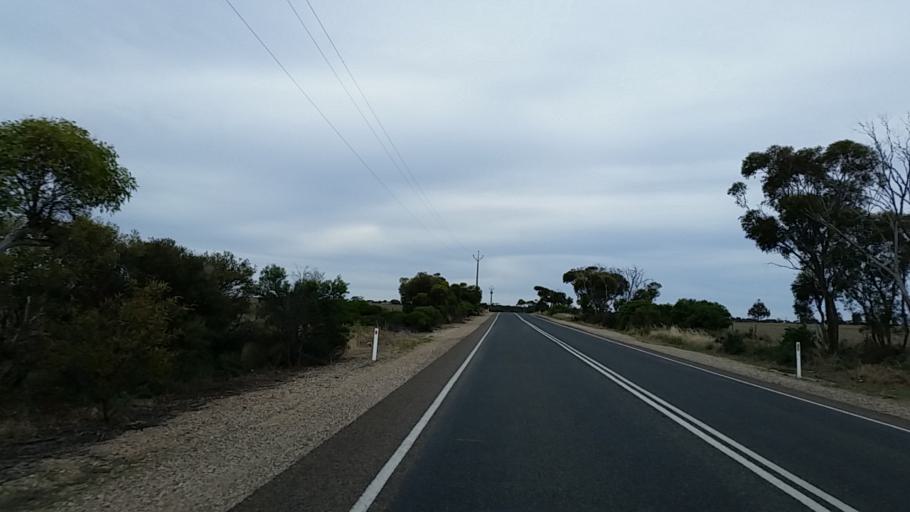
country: AU
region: South Australia
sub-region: Mid Murray
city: Mannum
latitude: -34.9094
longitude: 139.2746
